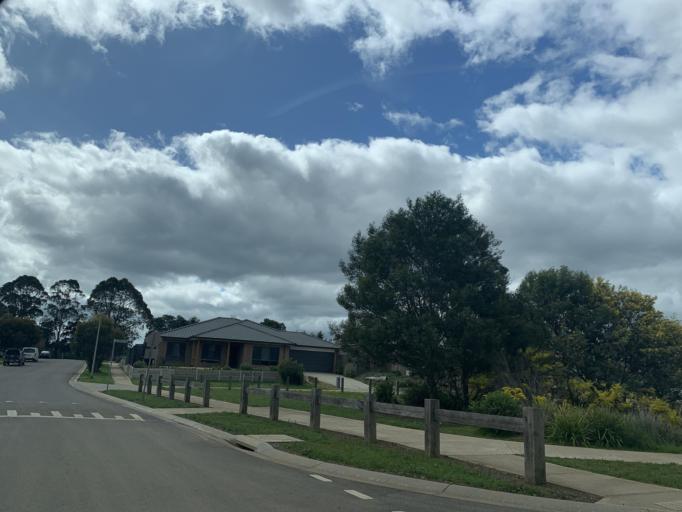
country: AU
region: Victoria
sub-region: Whittlesea
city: Whittlesea
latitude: -37.2885
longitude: 144.9360
